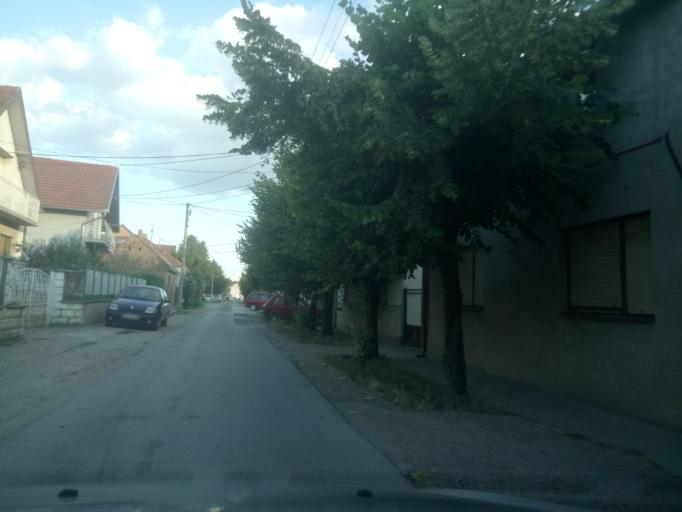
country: RS
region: Autonomna Pokrajina Vojvodina
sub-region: Sremski Okrug
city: Ingija
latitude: 45.0571
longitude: 20.0790
